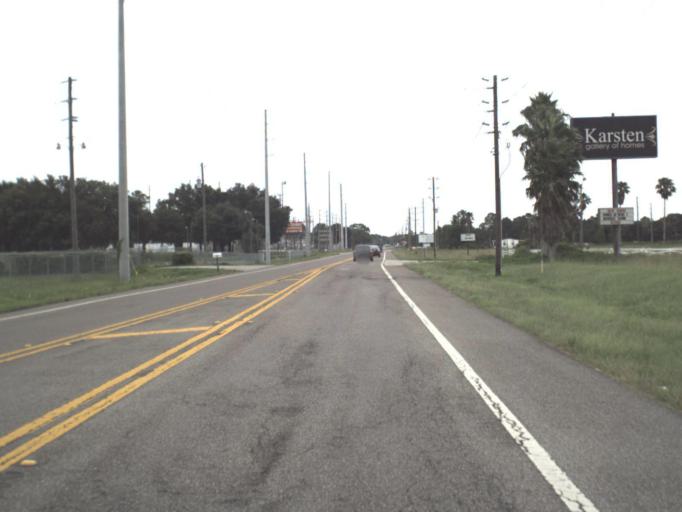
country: US
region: Florida
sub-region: Pasco County
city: Zephyrhills West
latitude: 28.2202
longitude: -82.2404
